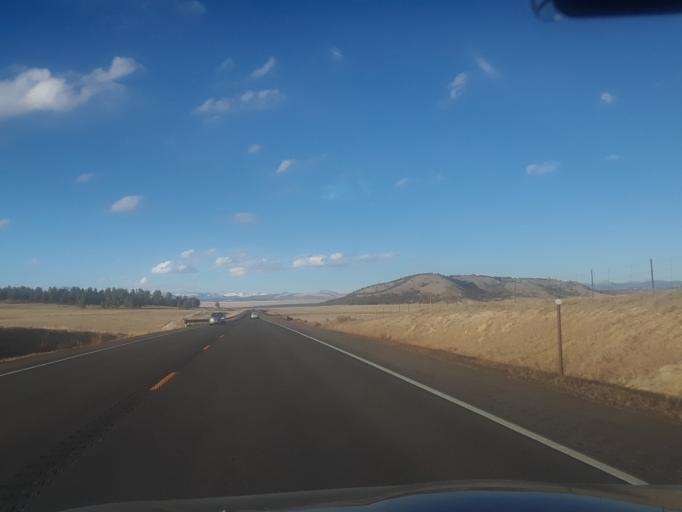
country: US
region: Colorado
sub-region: Chaffee County
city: Buena Vista
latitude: 38.9334
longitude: -105.9660
